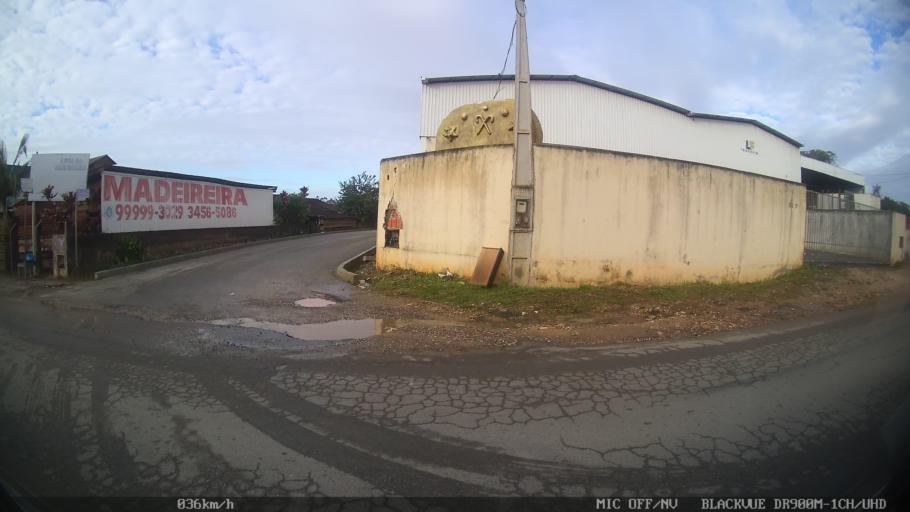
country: BR
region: Santa Catarina
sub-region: Barra Velha
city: Barra Velha
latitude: -26.6203
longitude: -48.7130
